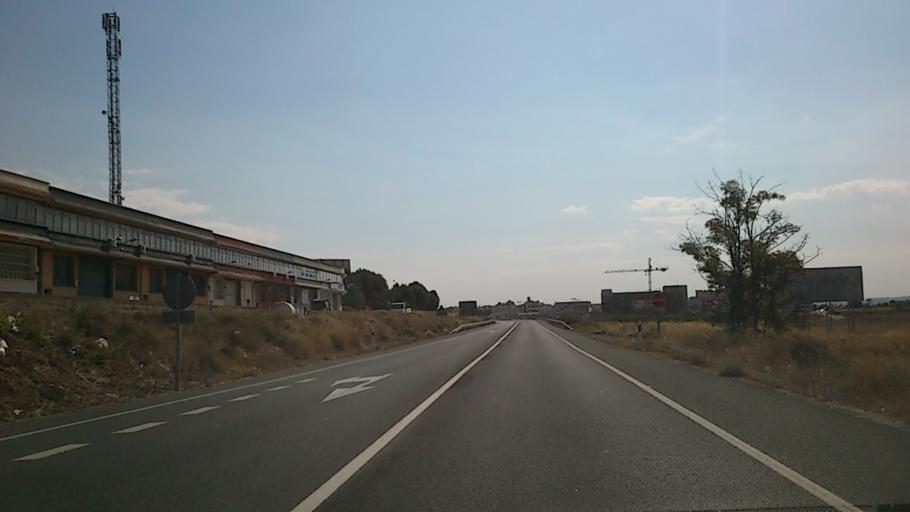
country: ES
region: Aragon
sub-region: Provincia de Zaragoza
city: Puebla de Alfinden
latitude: 41.6375
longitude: -0.7627
